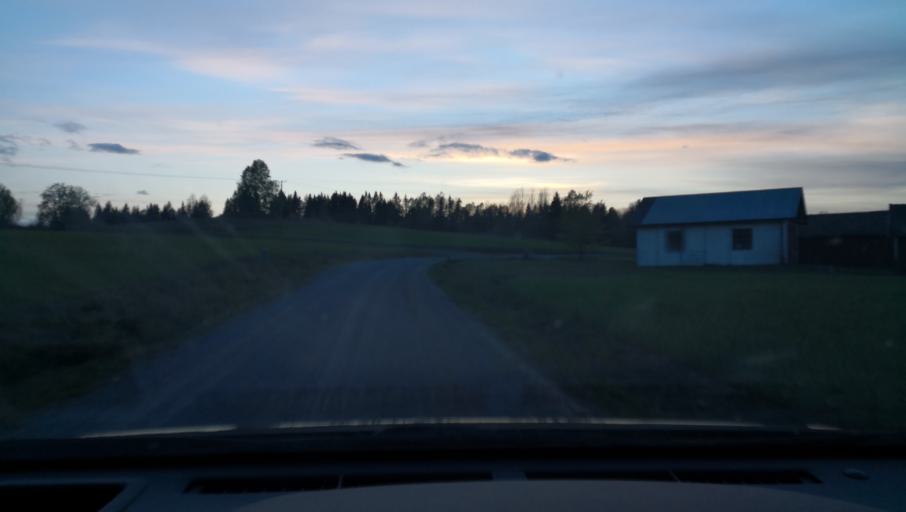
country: SE
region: OErebro
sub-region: Askersunds Kommun
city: Askersund
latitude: 58.9905
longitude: 14.9084
